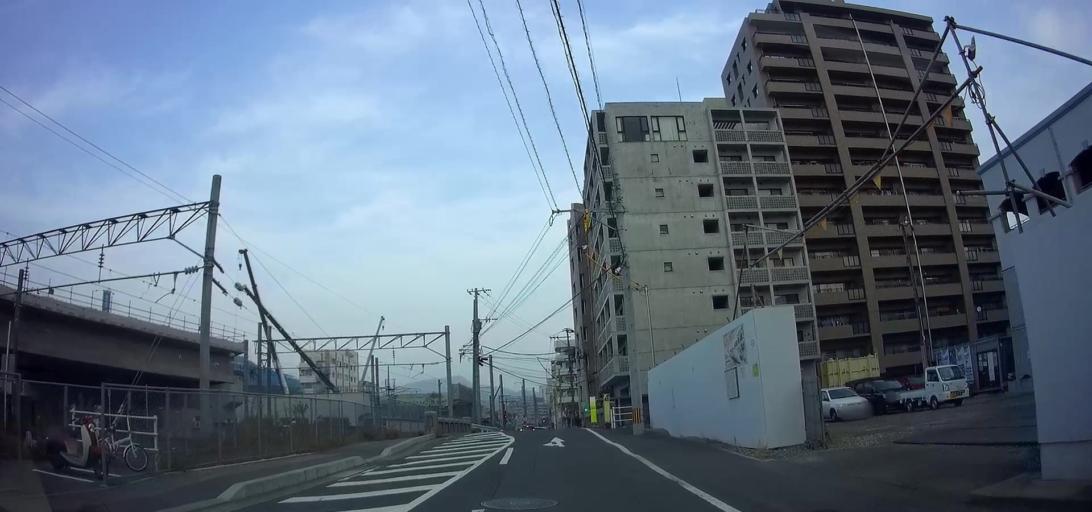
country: JP
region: Nagasaki
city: Nagasaki-shi
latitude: 32.7564
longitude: 129.8686
